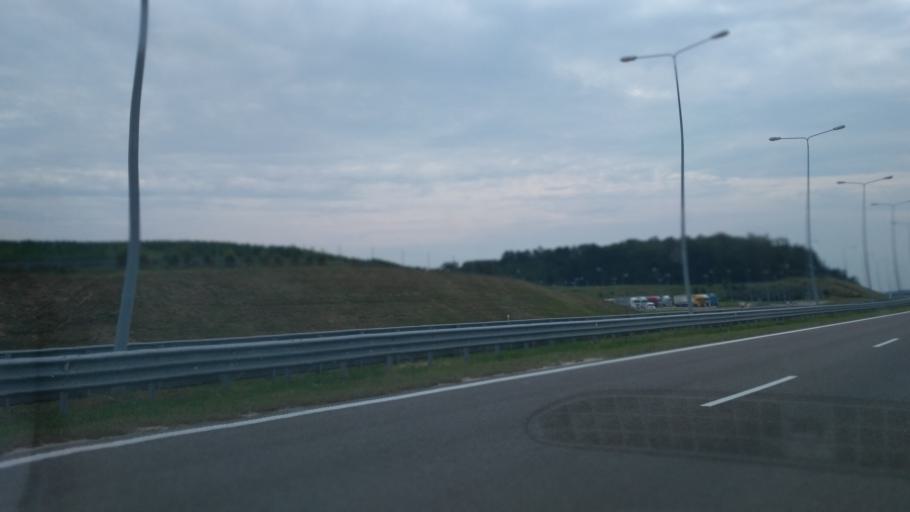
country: PL
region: Subcarpathian Voivodeship
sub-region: Powiat jaroslawski
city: Wierzbna
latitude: 49.9968
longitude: 22.6044
